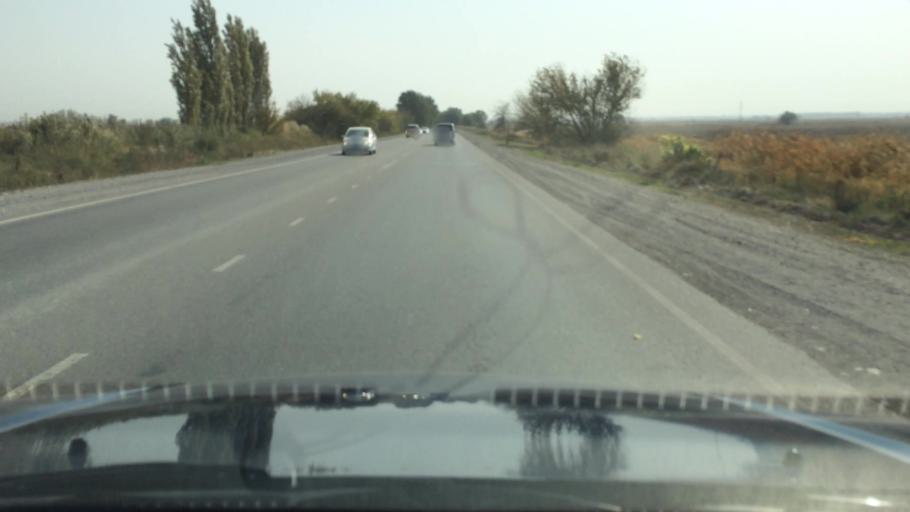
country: KG
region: Chuy
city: Lebedinovka
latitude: 42.9253
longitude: 74.7008
